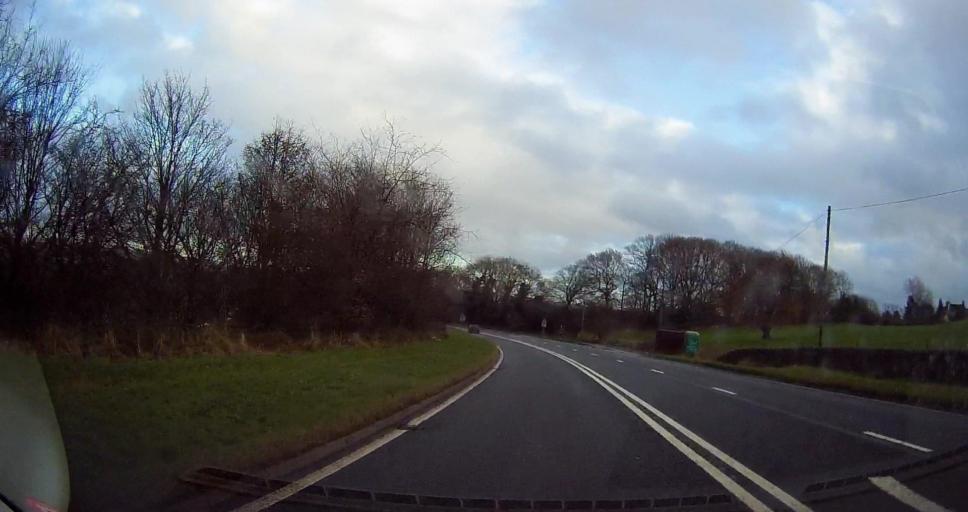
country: GB
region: England
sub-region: Derbyshire
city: Wingerworth
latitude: 53.2297
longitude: -1.5087
